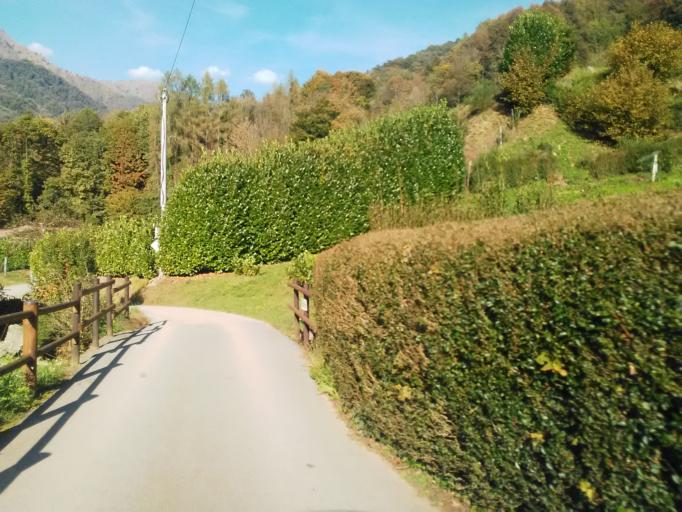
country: IT
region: Piedmont
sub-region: Provincia di Vercelli
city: Postua
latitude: 45.7231
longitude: 8.2187
